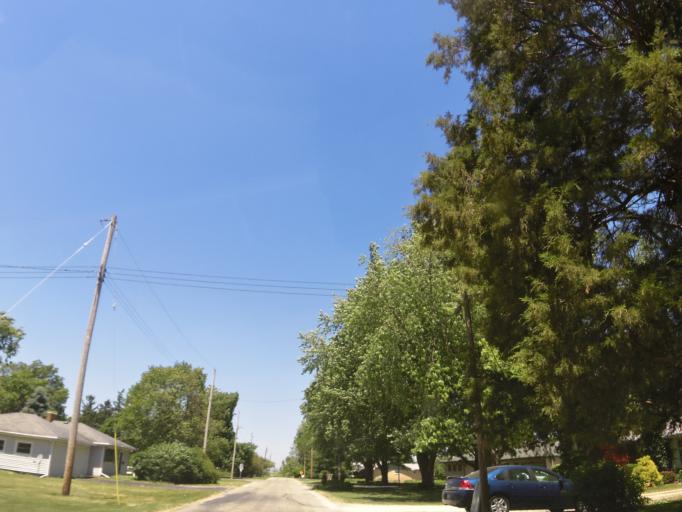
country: US
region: Illinois
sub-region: Livingston County
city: Chatsworth
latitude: 40.7567
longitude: -88.1833
